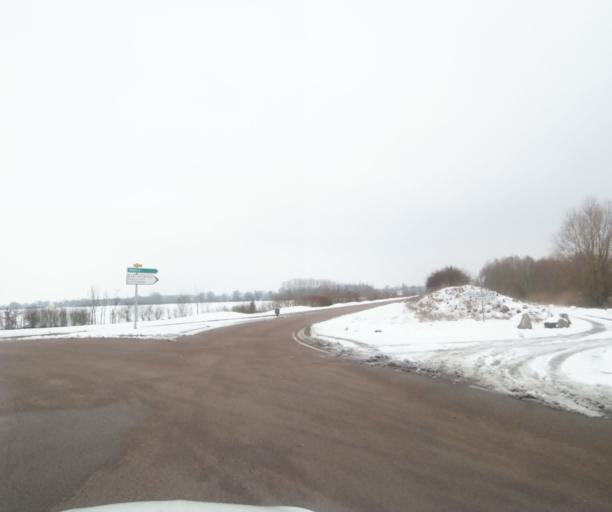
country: FR
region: Champagne-Ardenne
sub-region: Departement de la Haute-Marne
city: Saint-Dizier
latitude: 48.5841
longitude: 4.8887
